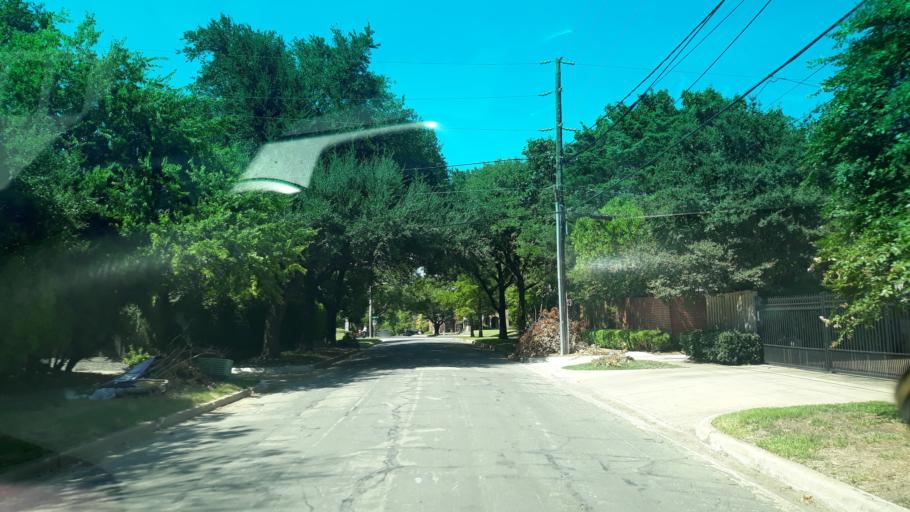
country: US
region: Texas
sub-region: Dallas County
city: Highland Park
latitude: 32.8183
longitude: -96.7464
